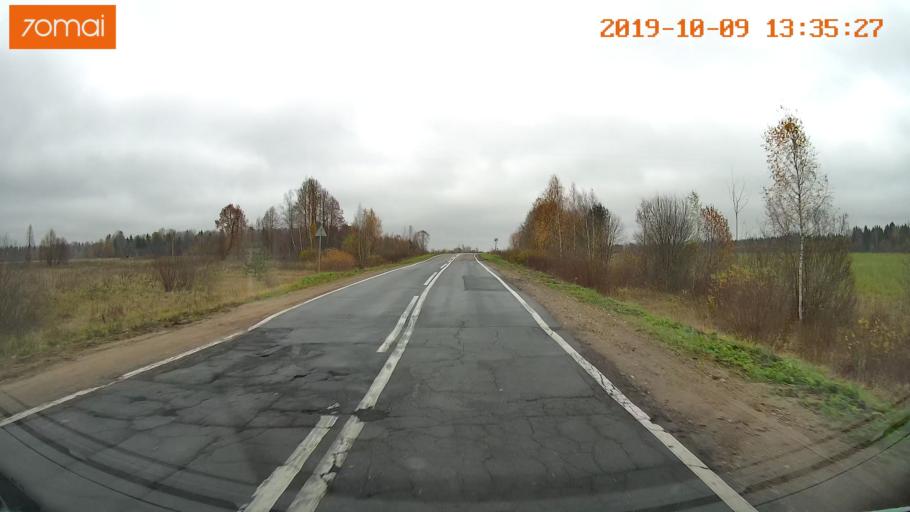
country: RU
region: Jaroslavl
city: Lyubim
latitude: 58.3364
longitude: 41.0784
